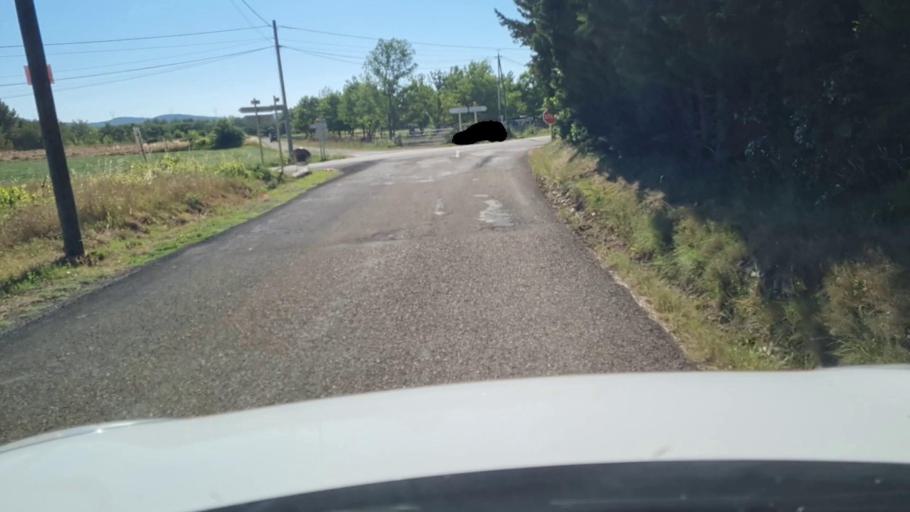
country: FR
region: Languedoc-Roussillon
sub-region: Departement du Gard
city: Sommieres
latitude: 43.8318
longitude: 4.0393
